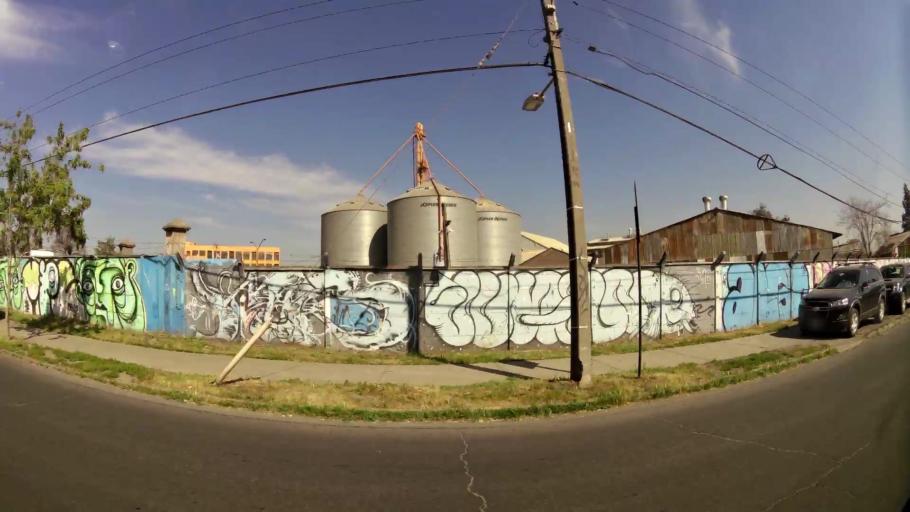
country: CL
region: Santiago Metropolitan
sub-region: Provincia de Maipo
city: San Bernardo
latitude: -33.5979
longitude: -70.6950
